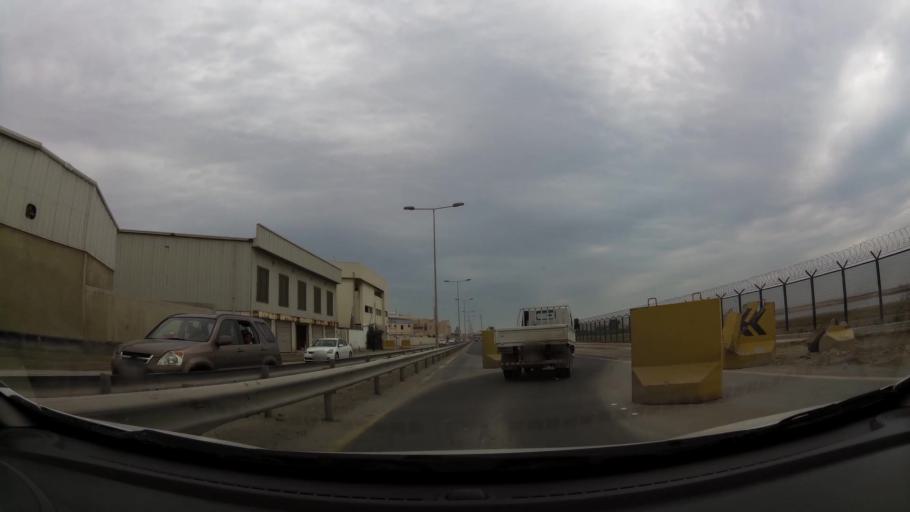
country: BH
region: Northern
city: Sitrah
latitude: 26.1495
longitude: 50.6199
